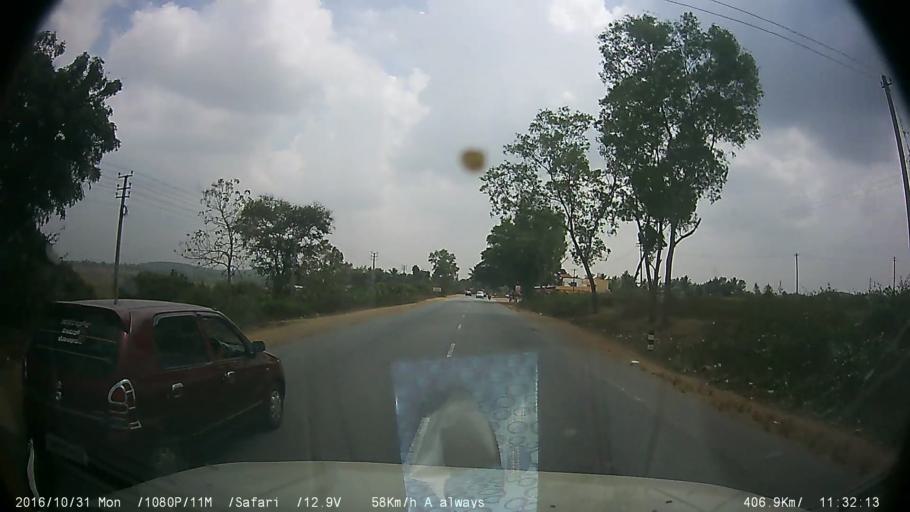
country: IN
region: Karnataka
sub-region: Mysore
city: Hunsur
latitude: 12.3141
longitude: 76.2499
